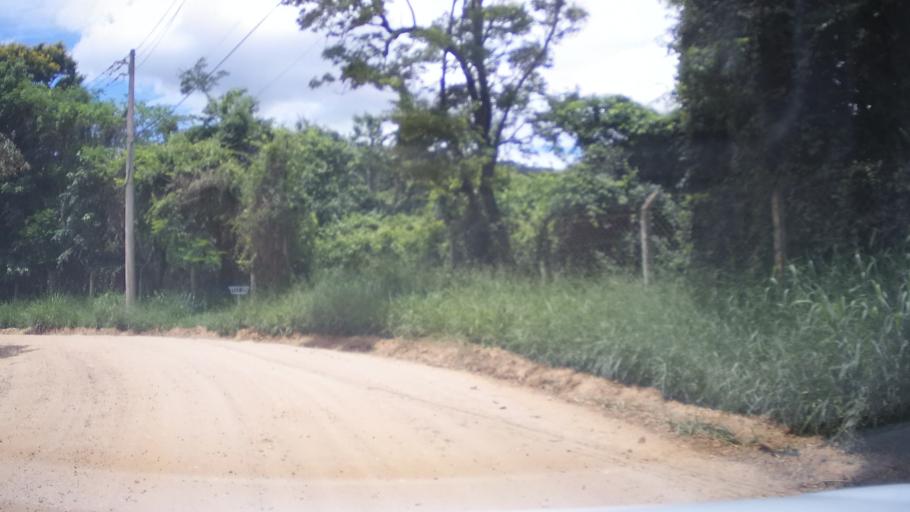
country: BR
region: Sao Paulo
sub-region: Vinhedo
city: Vinhedo
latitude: -22.9987
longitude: -46.9598
